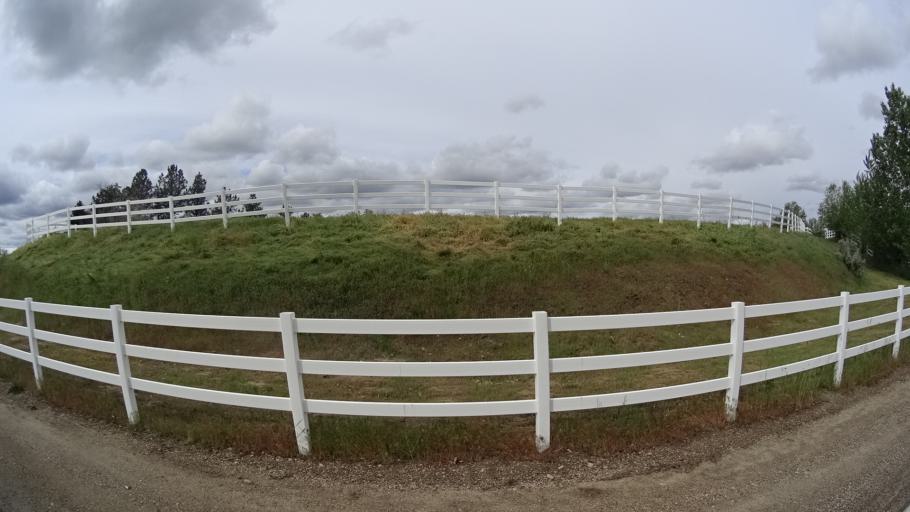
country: US
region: Idaho
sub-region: Ada County
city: Eagle
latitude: 43.7336
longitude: -116.3567
